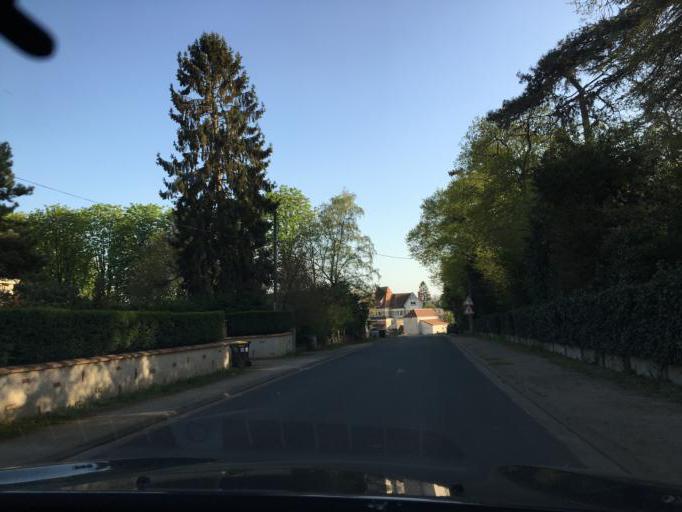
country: FR
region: Centre
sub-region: Departement du Loir-et-Cher
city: Ouzouer-le-Marche
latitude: 47.9142
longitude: 1.5248
